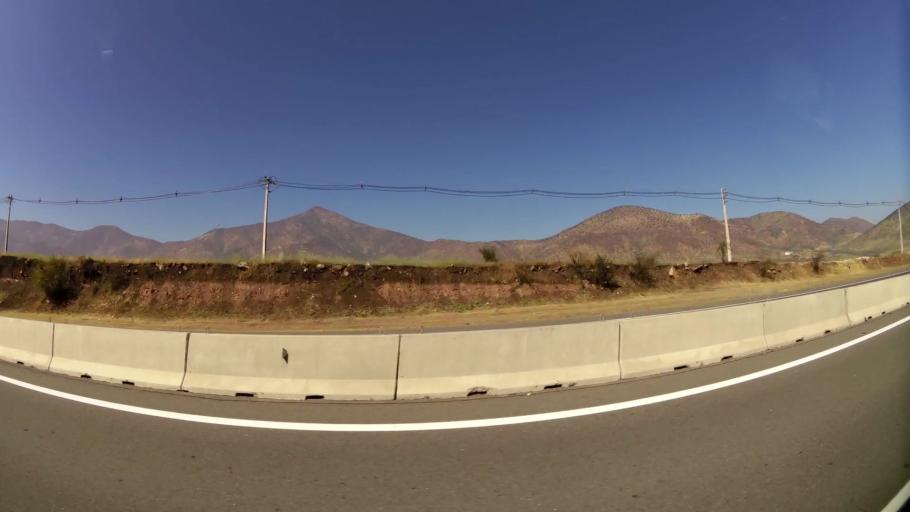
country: CL
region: Santiago Metropolitan
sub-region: Provincia de Chacabuco
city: Chicureo Abajo
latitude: -33.3126
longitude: -70.6474
